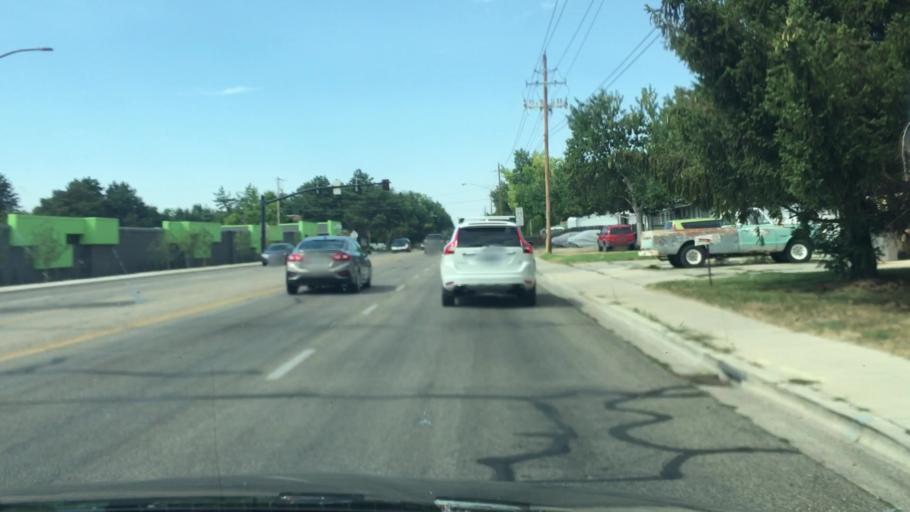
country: US
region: Idaho
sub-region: Ada County
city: Garden City
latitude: 43.6272
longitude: -116.2742
